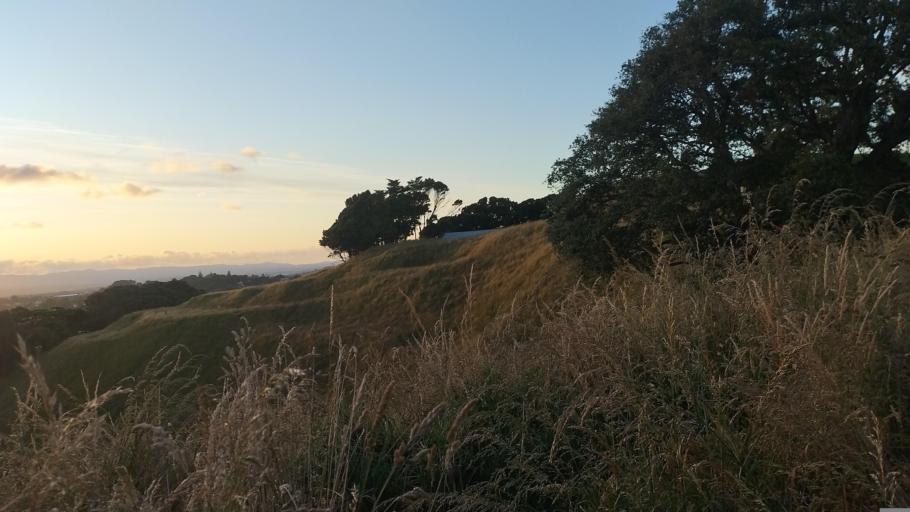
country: NZ
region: Auckland
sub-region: Auckland
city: Auckland
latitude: -36.9011
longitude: 174.7815
